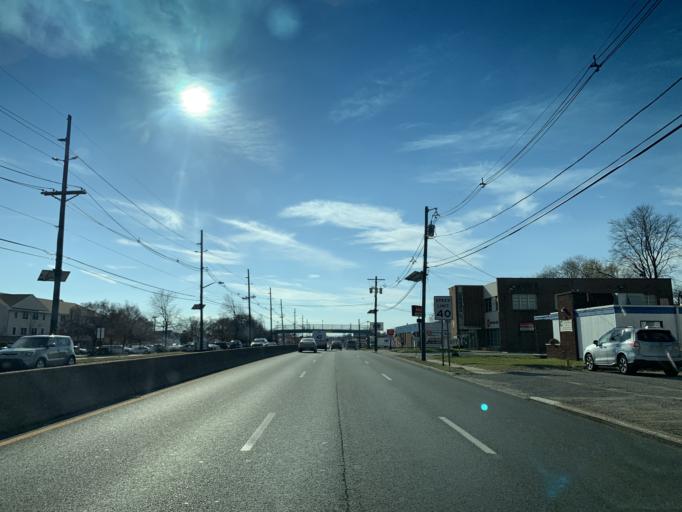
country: US
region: New Jersey
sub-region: Camden County
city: Merchantville
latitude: 39.9453
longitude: -75.0691
